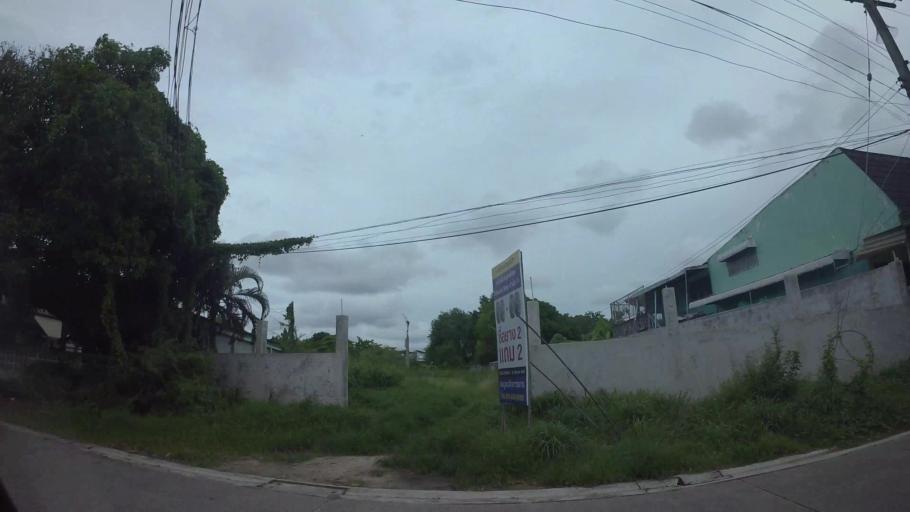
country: TH
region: Rayong
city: Rayong
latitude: 12.6821
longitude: 101.2732
